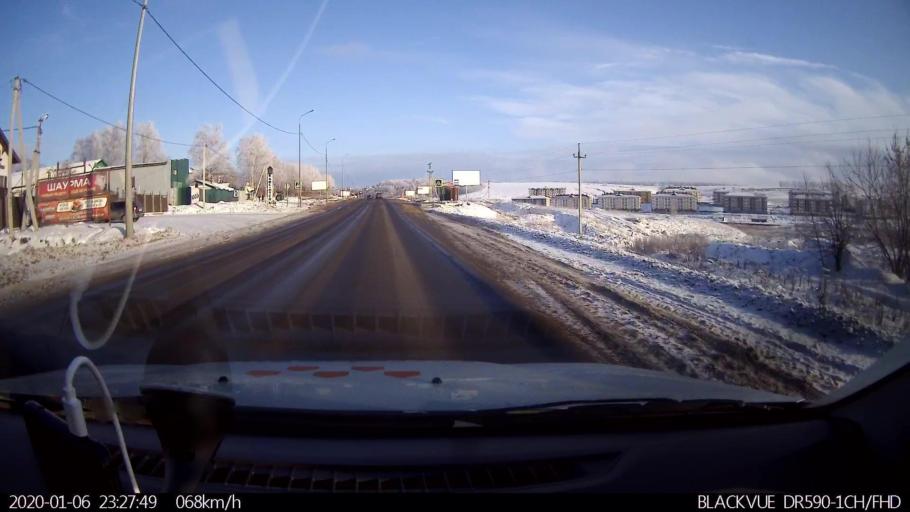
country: RU
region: Nizjnij Novgorod
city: Burevestnik
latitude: 56.2121
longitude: 43.8925
